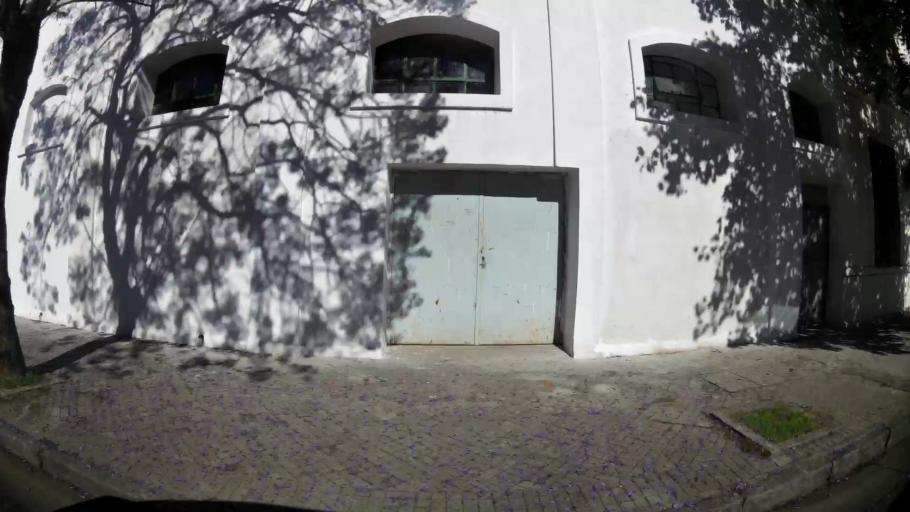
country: AR
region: Santa Fe
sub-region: Departamento de Rosario
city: Rosario
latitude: -32.9519
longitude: -60.6654
